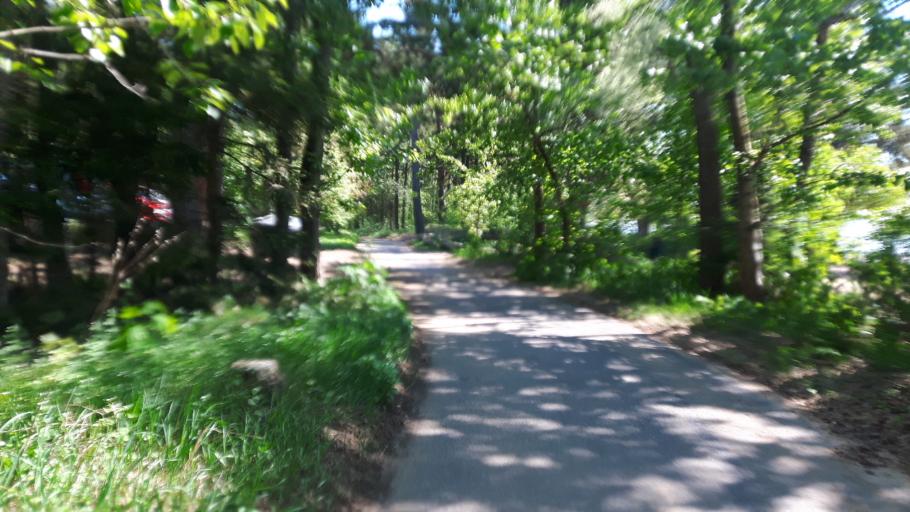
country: RU
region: St.-Petersburg
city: Komarovo
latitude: 60.1783
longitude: 29.7836
